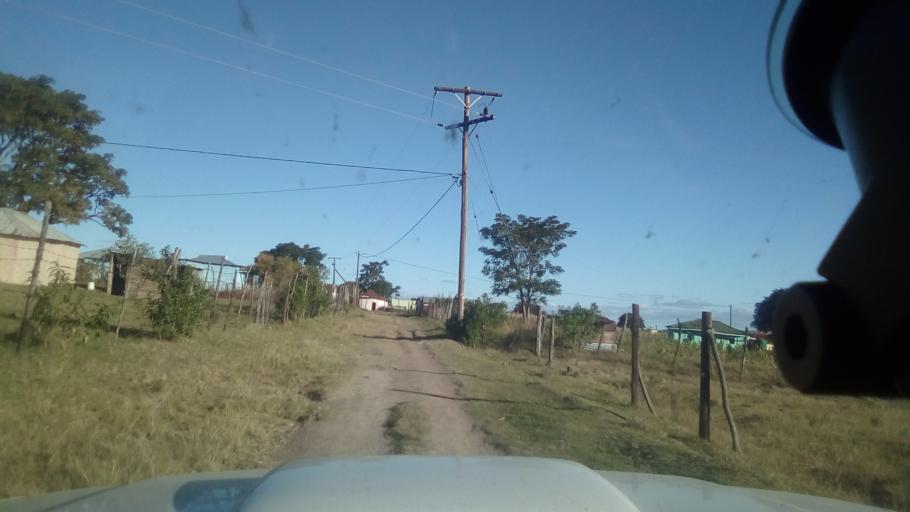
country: ZA
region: Eastern Cape
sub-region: Buffalo City Metropolitan Municipality
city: Bhisho
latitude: -32.7338
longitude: 27.3659
